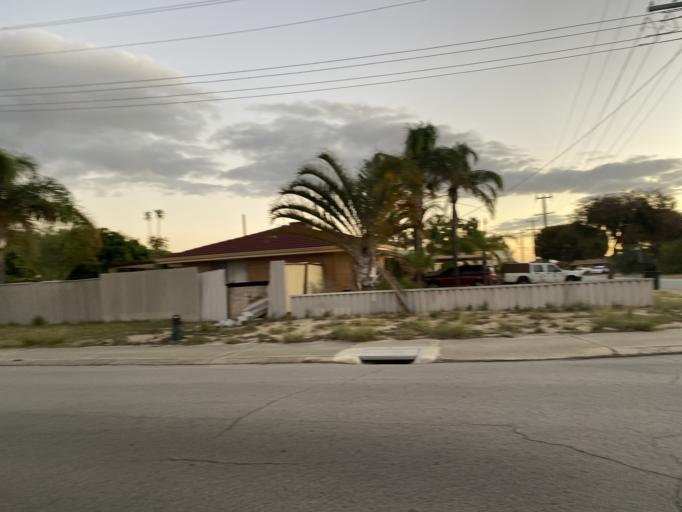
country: AU
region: Western Australia
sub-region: Belmont
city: Kewdale
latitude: -31.9865
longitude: 115.9927
